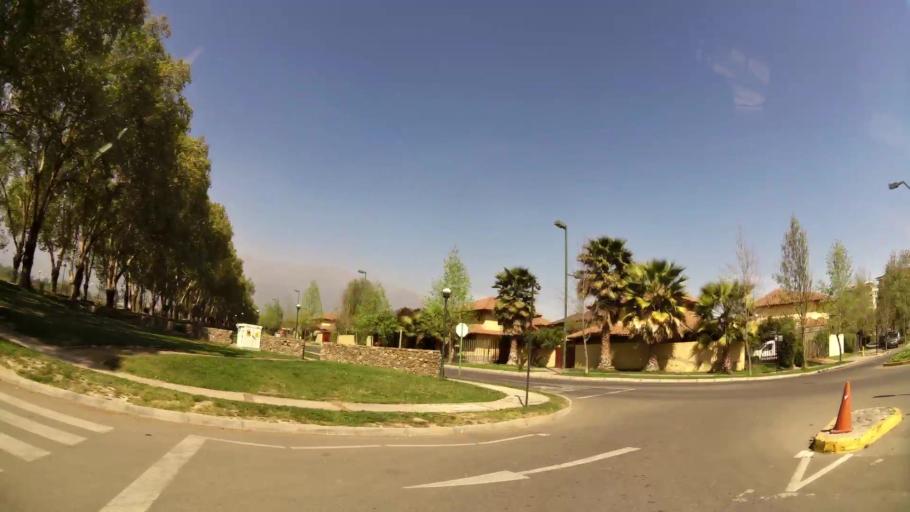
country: CL
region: Santiago Metropolitan
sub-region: Provincia de Santiago
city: Villa Presidente Frei, Nunoa, Santiago, Chile
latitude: -33.4861
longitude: -70.5753
